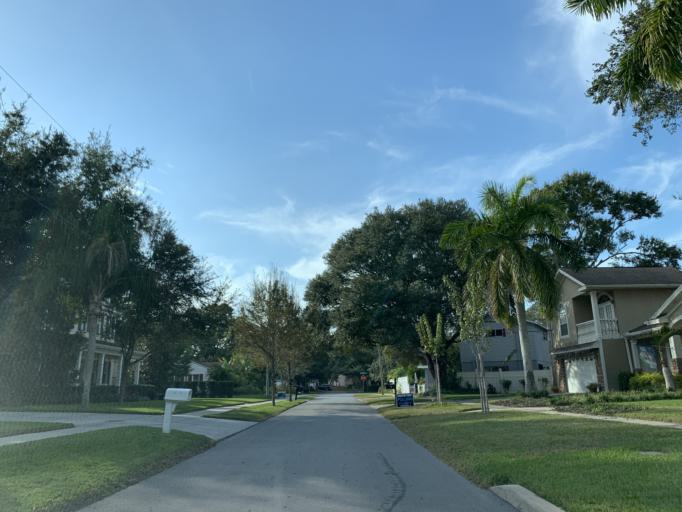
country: US
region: Florida
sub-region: Hillsborough County
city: Tampa
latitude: 27.9051
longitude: -82.4994
